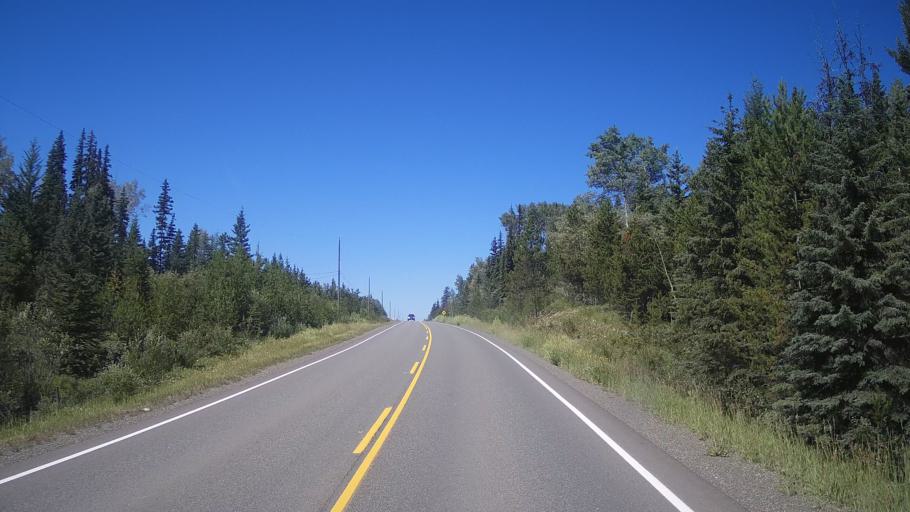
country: CA
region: British Columbia
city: Cache Creek
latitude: 51.5418
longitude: -120.9687
